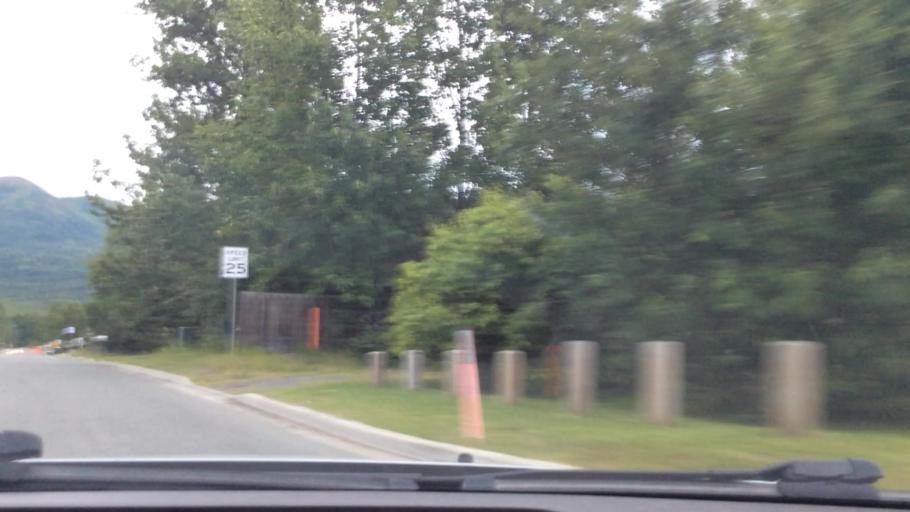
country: US
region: Alaska
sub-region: Anchorage Municipality
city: Elmendorf Air Force Base
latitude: 61.1919
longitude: -149.7331
